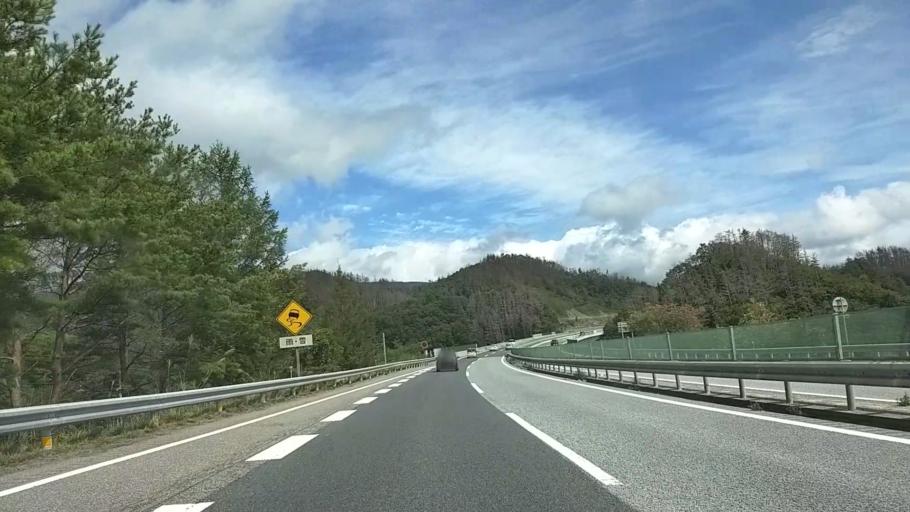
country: JP
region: Nagano
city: Hotaka
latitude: 36.4310
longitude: 138.0105
